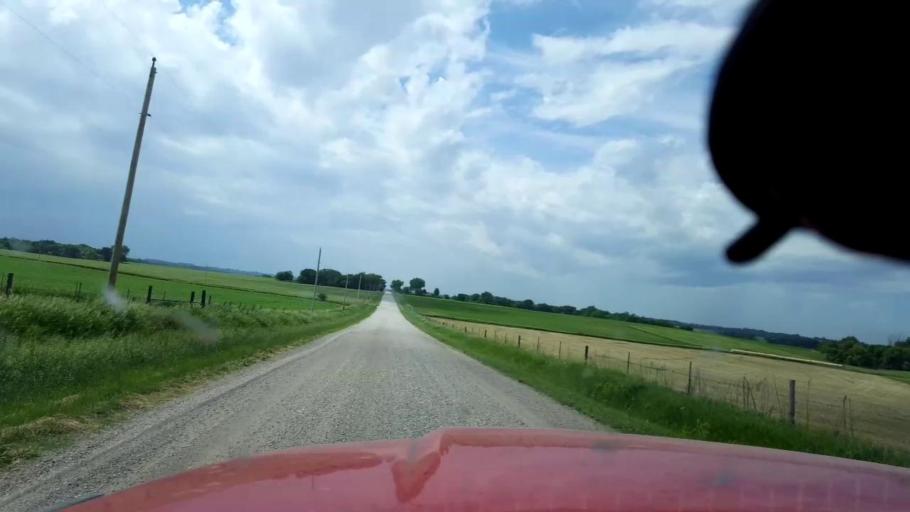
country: US
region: Iowa
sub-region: Cherokee County
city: Cherokee
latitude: 42.8168
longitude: -95.5345
